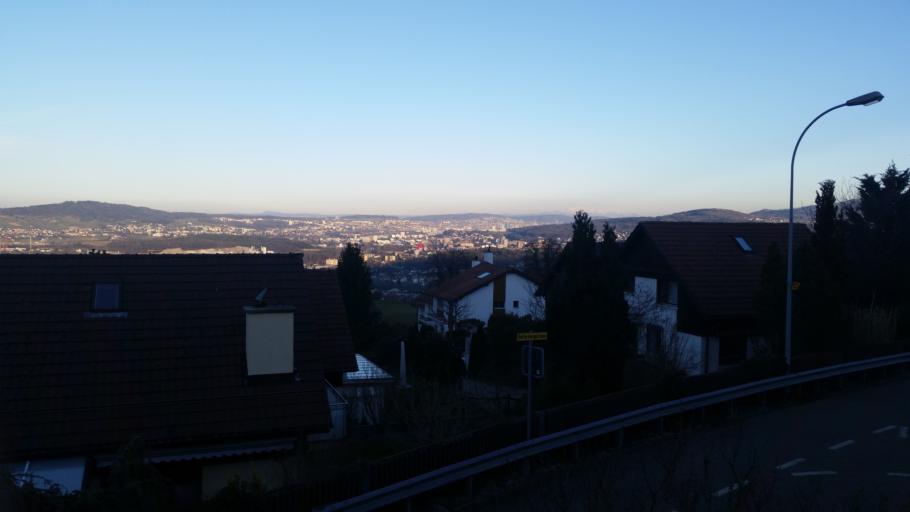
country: CH
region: Zurich
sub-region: Bezirk Dietikon
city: Dietikon / Almend
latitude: 47.3979
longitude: 8.3764
